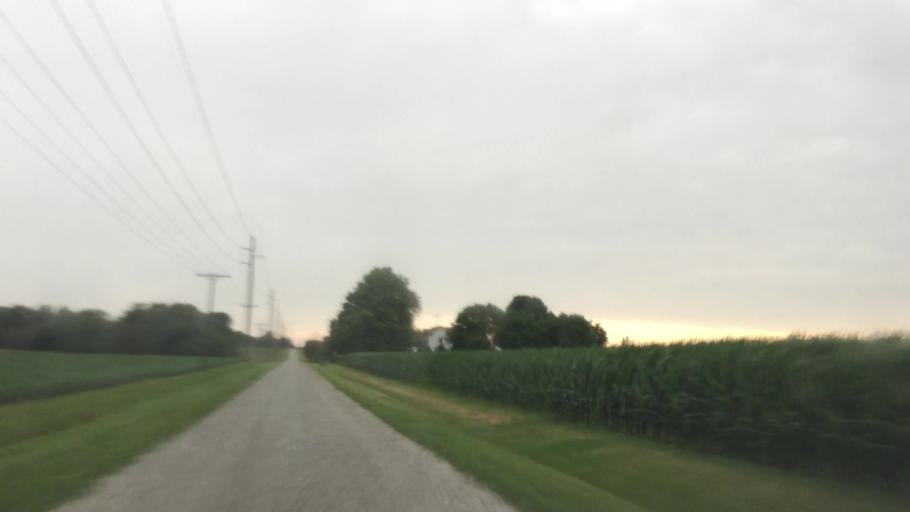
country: US
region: Iowa
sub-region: Lee County
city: Fort Madison
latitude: 40.5964
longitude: -91.2678
